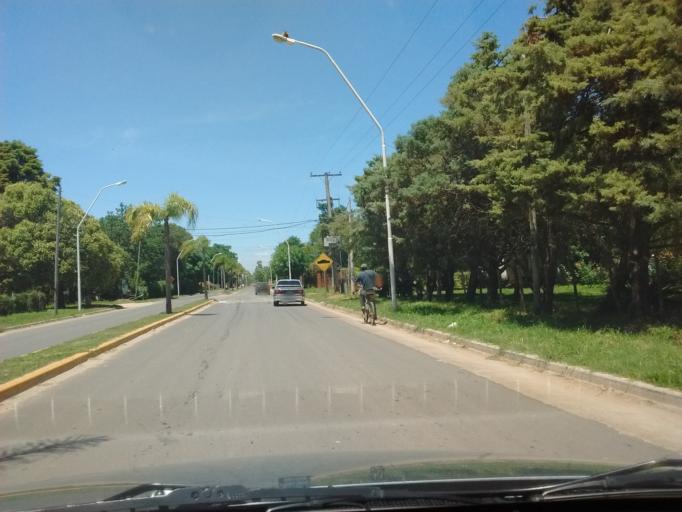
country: AR
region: Entre Rios
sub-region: Departamento de Gualeguay
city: Gualeguay
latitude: -33.1334
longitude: -59.3240
